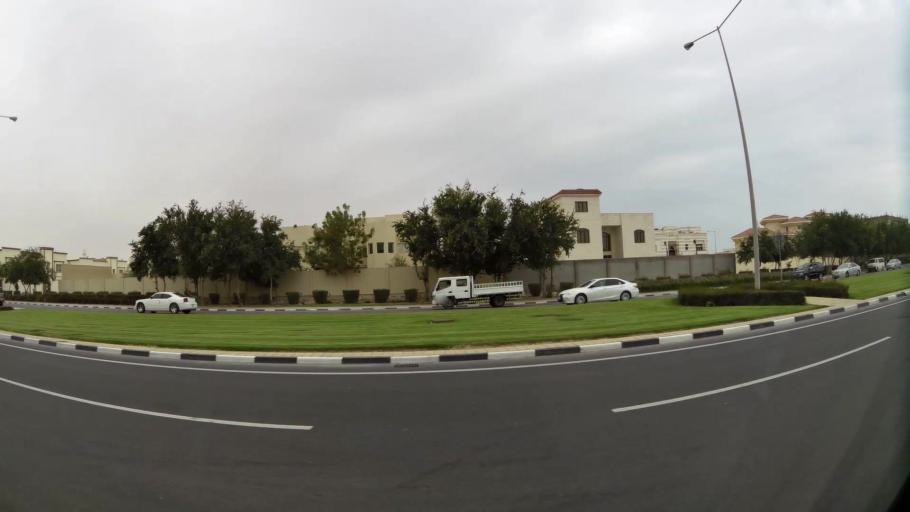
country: QA
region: Baladiyat ad Dawhah
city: Doha
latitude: 25.3484
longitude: 51.4962
